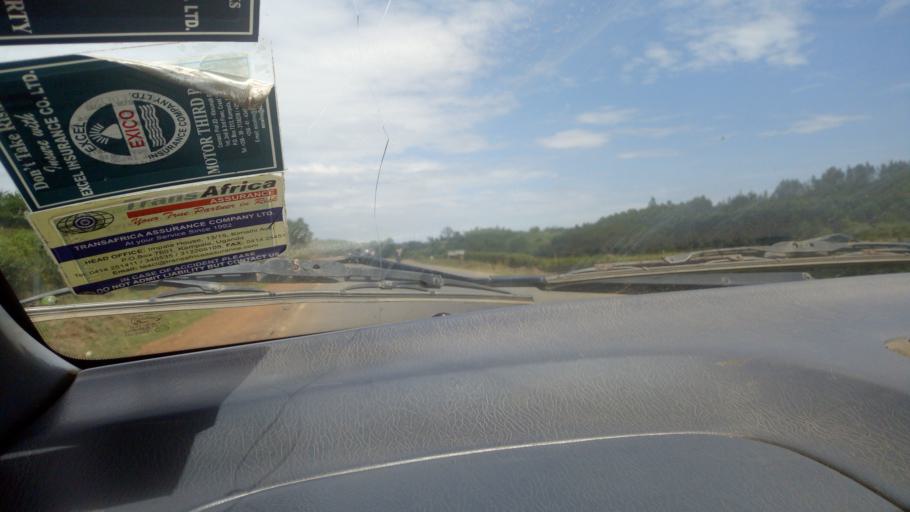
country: UG
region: Western Region
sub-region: Mbarara District
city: Bwizibwera
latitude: -0.3803
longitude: 30.5648
